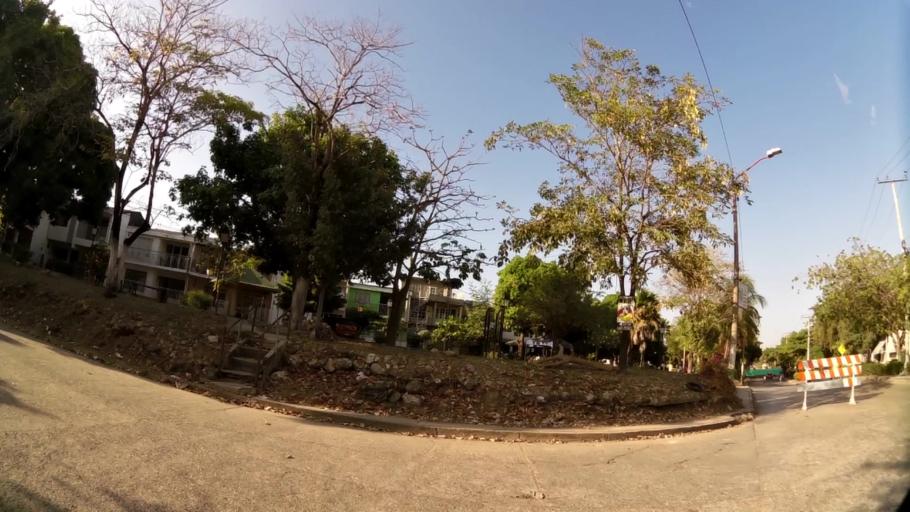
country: CO
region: Bolivar
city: Cartagena
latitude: 10.3798
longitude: -75.4797
